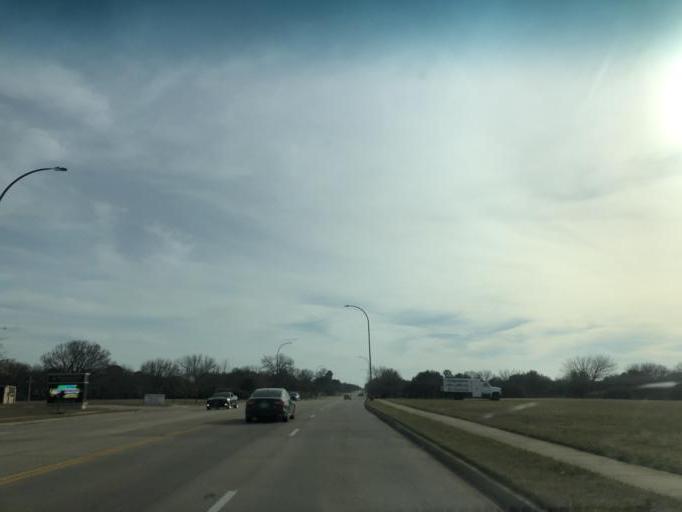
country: US
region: Texas
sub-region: Tarrant County
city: Dalworthington Gardens
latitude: 32.6987
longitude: -97.1494
